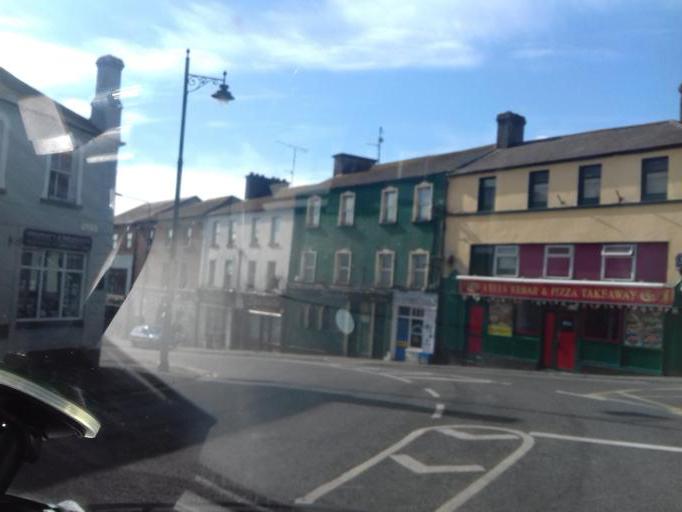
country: IE
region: Leinster
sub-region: An Mhi
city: Kells
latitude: 53.7273
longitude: -6.8768
